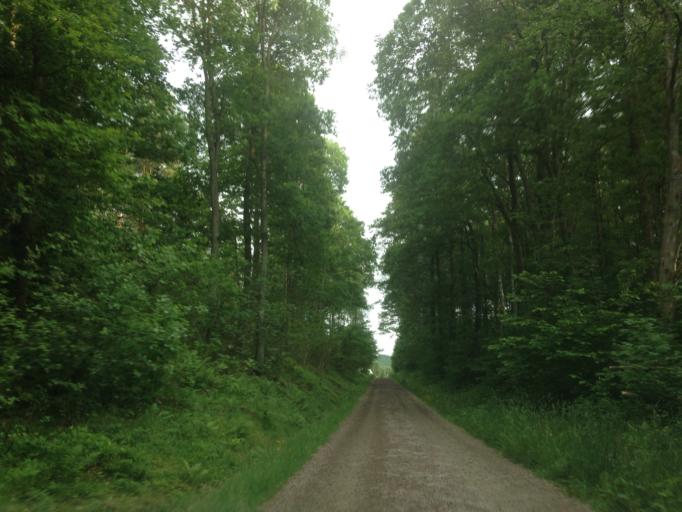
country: SE
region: Vaestra Goetaland
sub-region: Kungalvs Kommun
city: Kungalv
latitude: 57.8139
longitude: 11.9304
